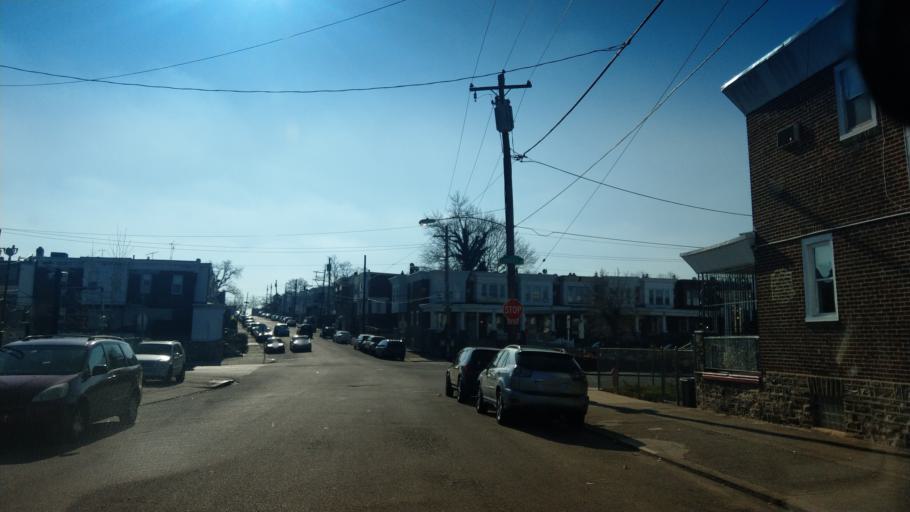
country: US
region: Pennsylvania
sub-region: Montgomery County
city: Rockledge
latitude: 40.0279
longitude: -75.1274
